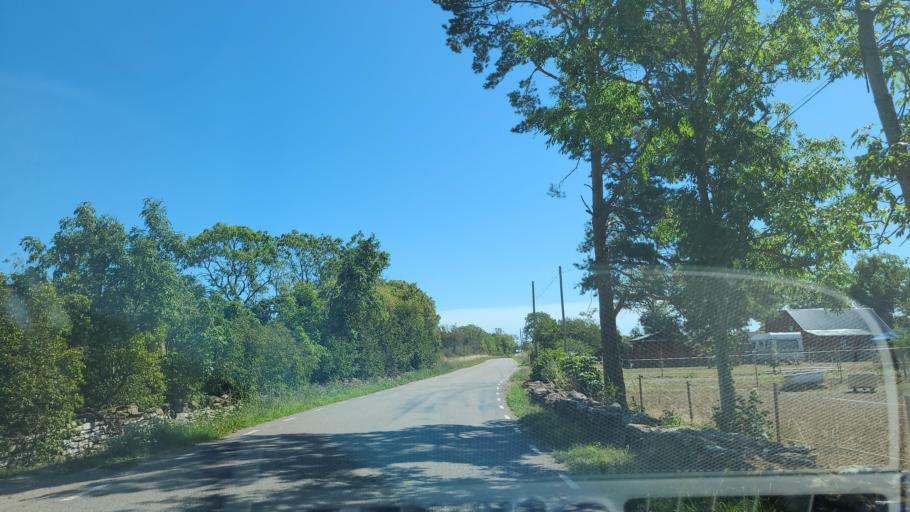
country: SE
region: Kalmar
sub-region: Borgholms Kommun
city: Borgholm
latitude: 56.7672
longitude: 16.6085
